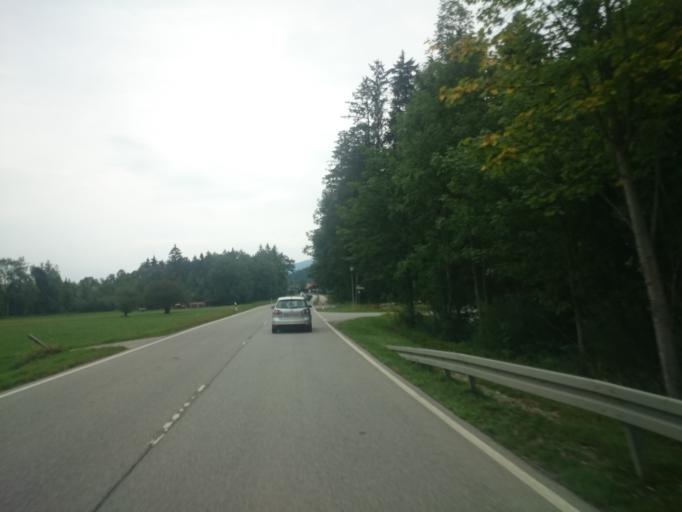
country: DE
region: Bavaria
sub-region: Upper Bavaria
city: Lenggries
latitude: 47.6311
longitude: 11.5942
